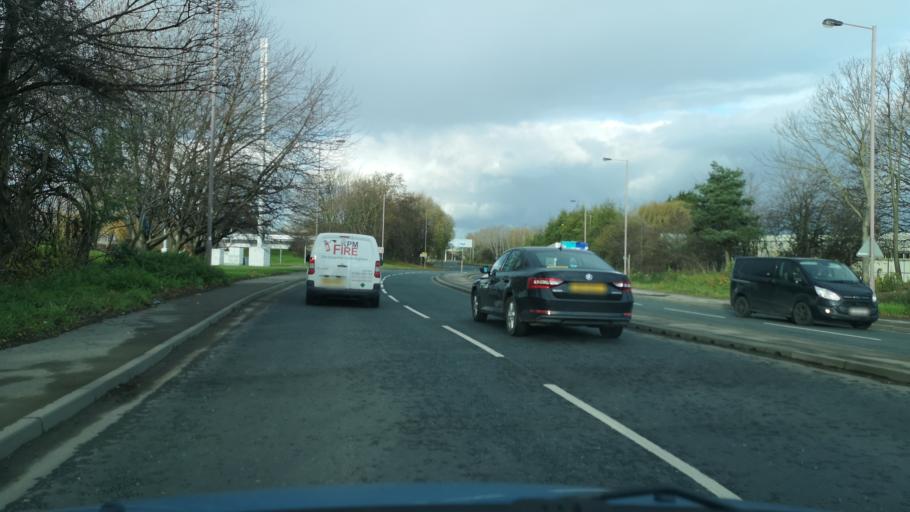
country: GB
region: England
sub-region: City and Borough of Wakefield
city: Normanton
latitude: 53.7048
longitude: -1.3970
